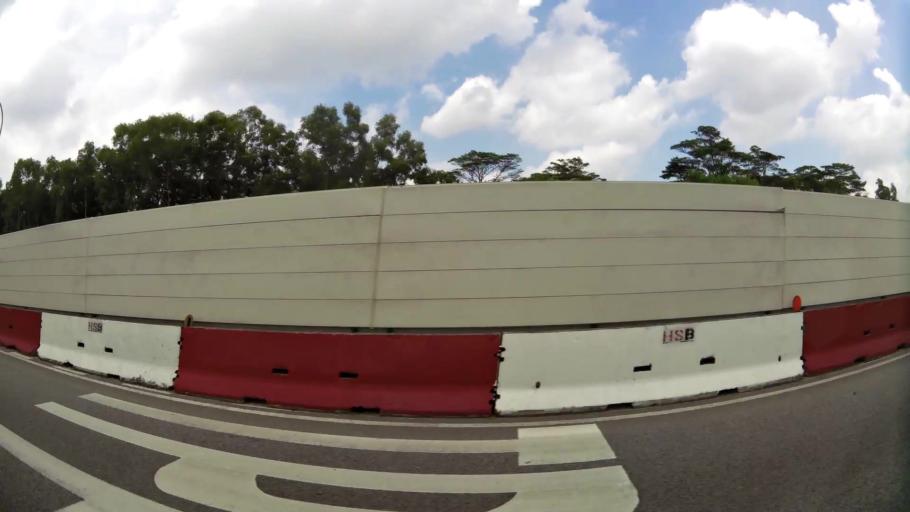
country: MY
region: Johor
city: Kampung Pasir Gudang Baru
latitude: 1.3786
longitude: 103.9130
